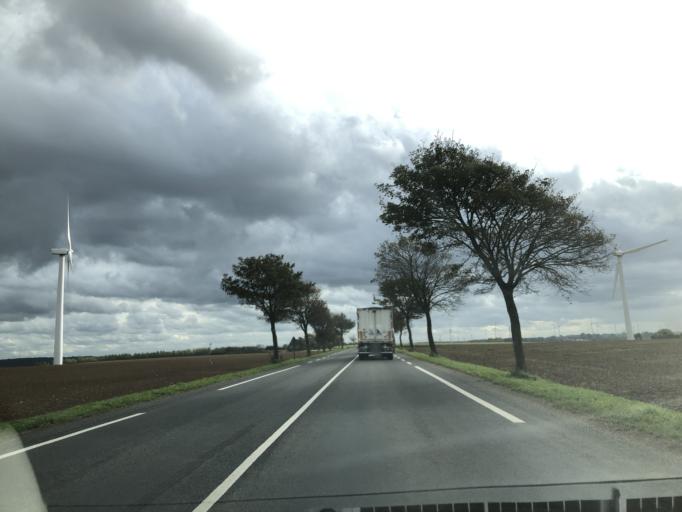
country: FR
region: Nord-Pas-de-Calais
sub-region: Departement du Pas-de-Calais
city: Wailly
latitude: 50.5725
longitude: 2.0957
